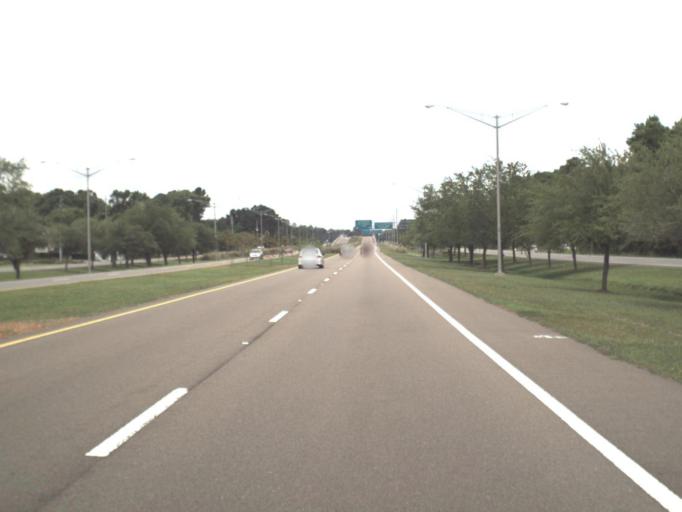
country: US
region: Florida
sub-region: Duval County
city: Jacksonville
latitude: 30.4832
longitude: -81.6535
